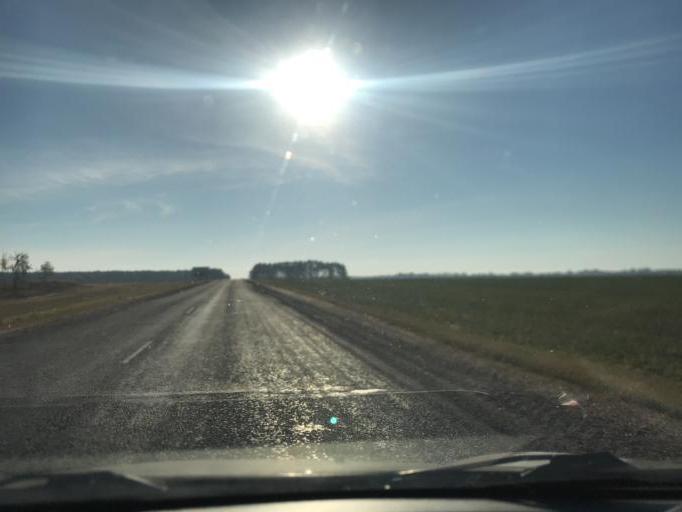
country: BY
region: Gomel
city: Khoyniki
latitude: 51.8179
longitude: 30.0874
